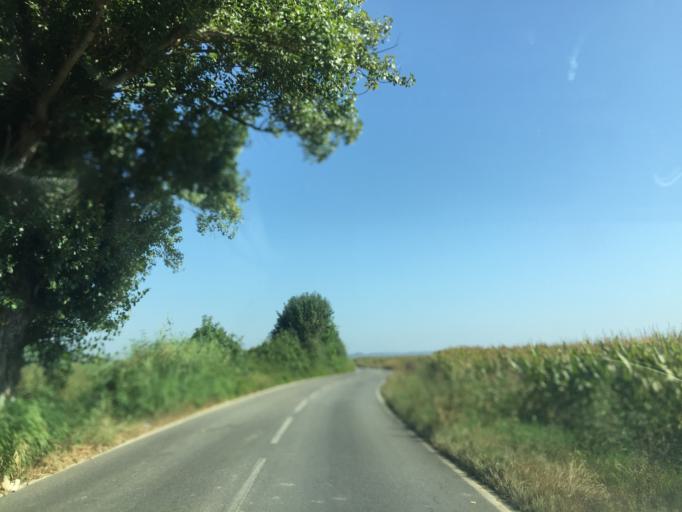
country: PT
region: Santarem
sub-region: Alpiarca
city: Alpiarca
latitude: 39.2942
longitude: -8.5234
